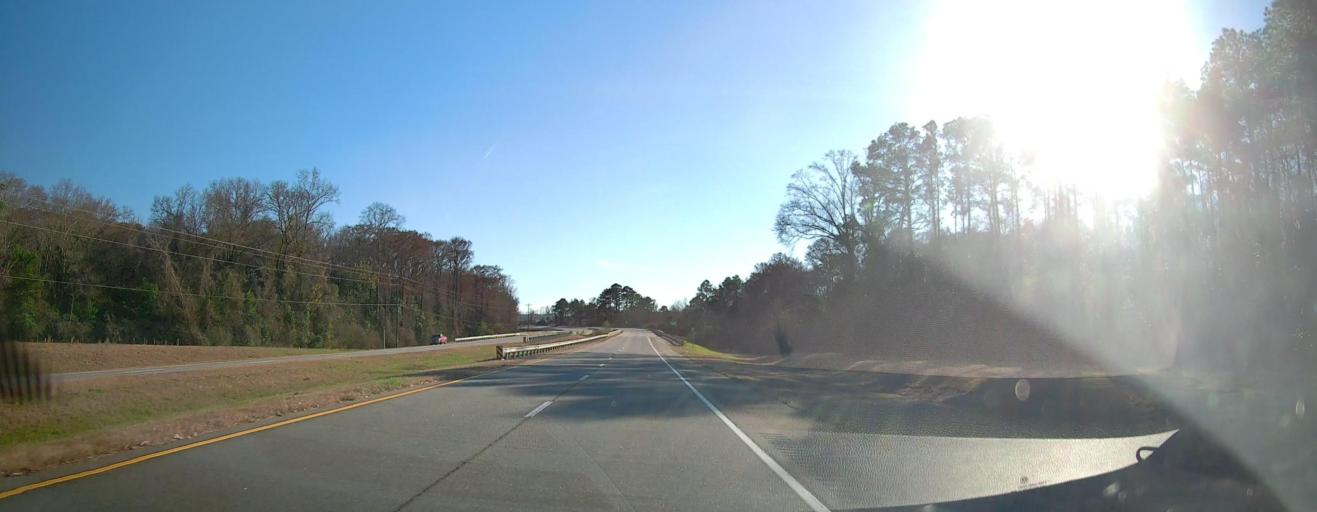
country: US
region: Georgia
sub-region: Sumter County
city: Americus
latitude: 31.9298
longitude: -84.2637
